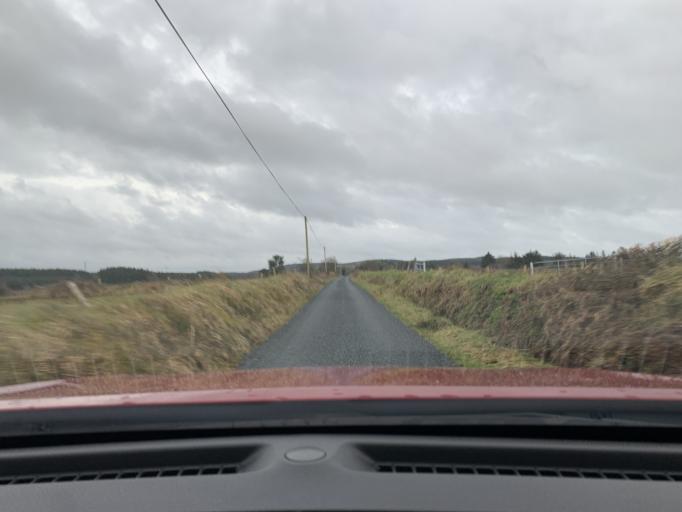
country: IE
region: Connaught
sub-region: Roscommon
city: Ballaghaderreen
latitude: 53.9702
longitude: -8.5260
